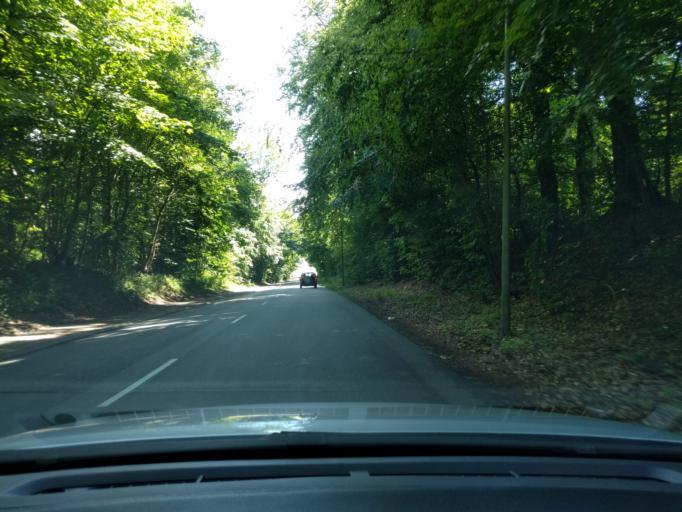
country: DK
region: South Denmark
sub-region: Middelfart Kommune
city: Middelfart
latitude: 55.5081
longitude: 9.7156
